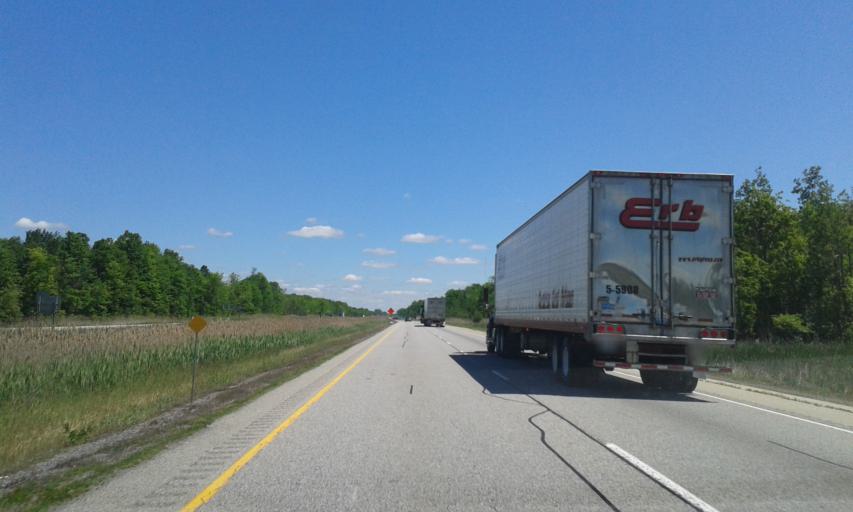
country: US
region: New York
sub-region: St. Lawrence County
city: Norfolk
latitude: 44.9238
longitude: -75.1810
